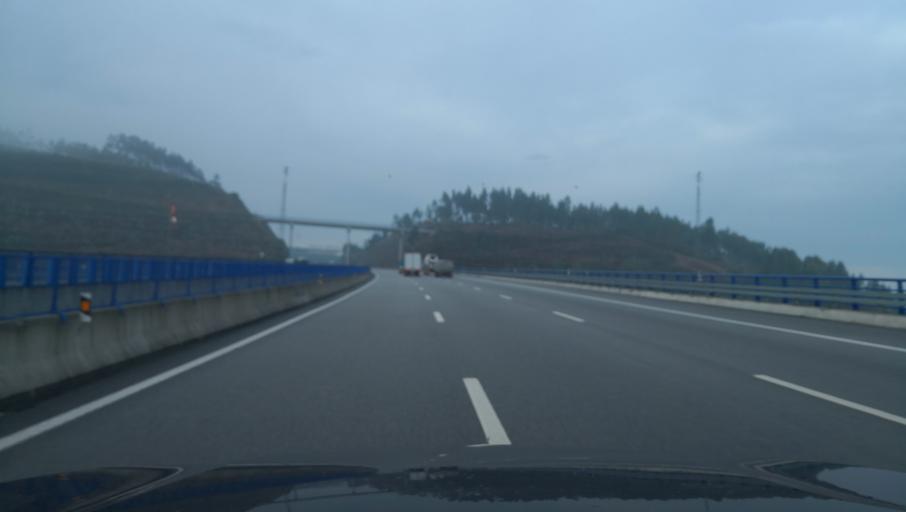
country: PT
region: Porto
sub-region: Paredes
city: Recarei
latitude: 41.1280
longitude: -8.4313
